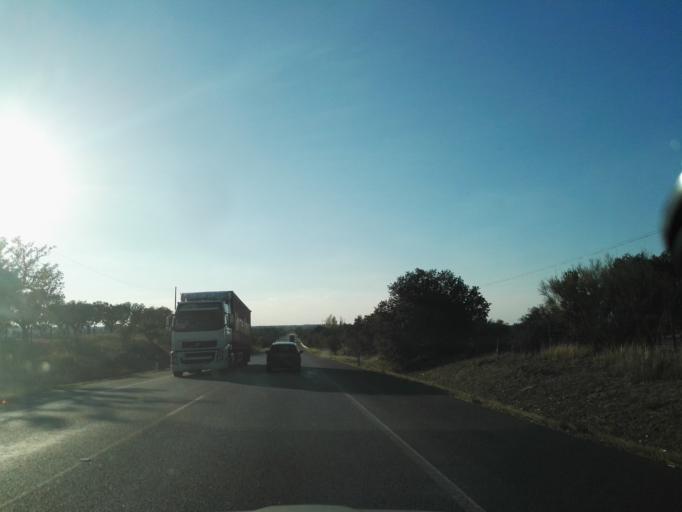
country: PT
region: Evora
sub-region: Estremoz
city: Estremoz
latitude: 38.8350
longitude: -7.7134
